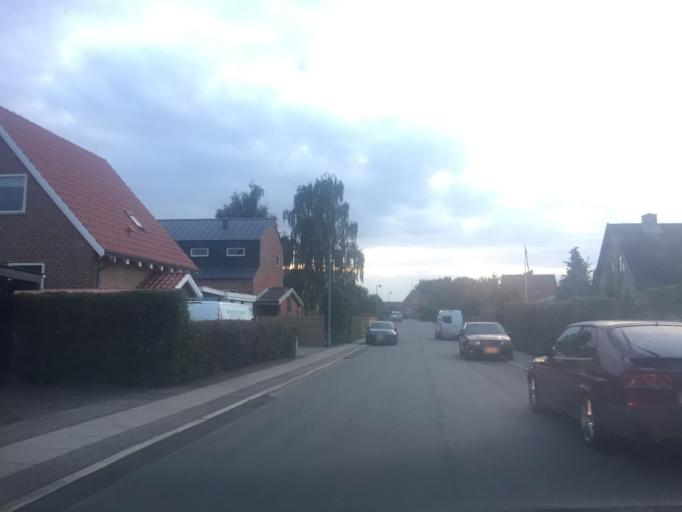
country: DK
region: Capital Region
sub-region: Hoje-Taastrup Kommune
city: Flong
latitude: 55.6525
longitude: 12.2029
